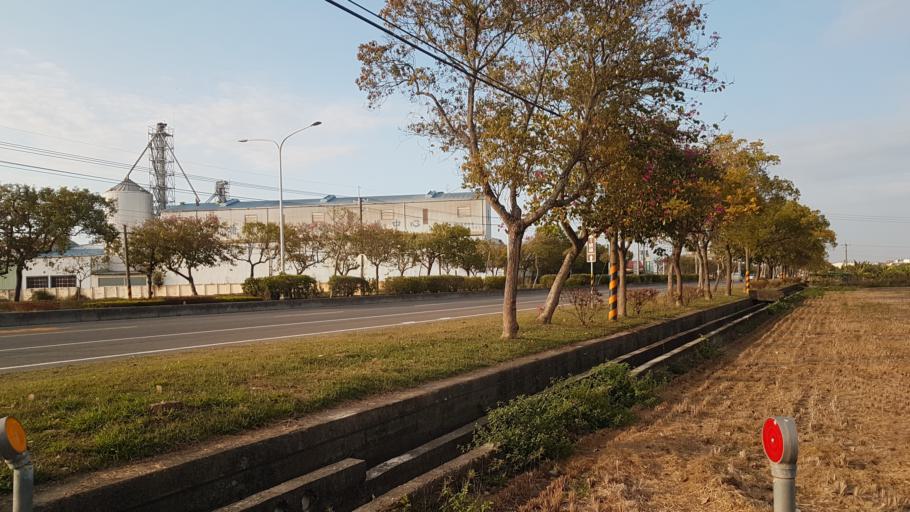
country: TW
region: Taiwan
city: Xinying
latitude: 23.3441
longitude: 120.3543
